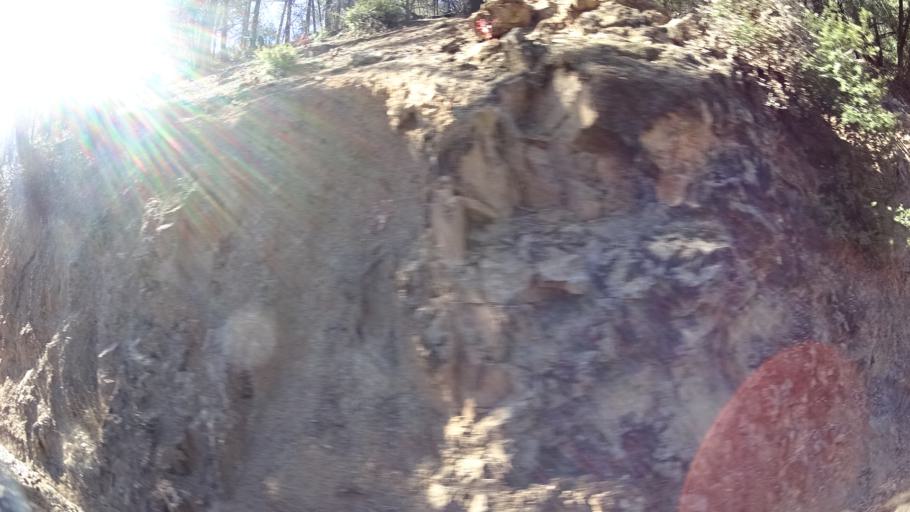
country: US
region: California
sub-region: Siskiyou County
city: Happy Camp
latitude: 41.3008
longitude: -123.1412
